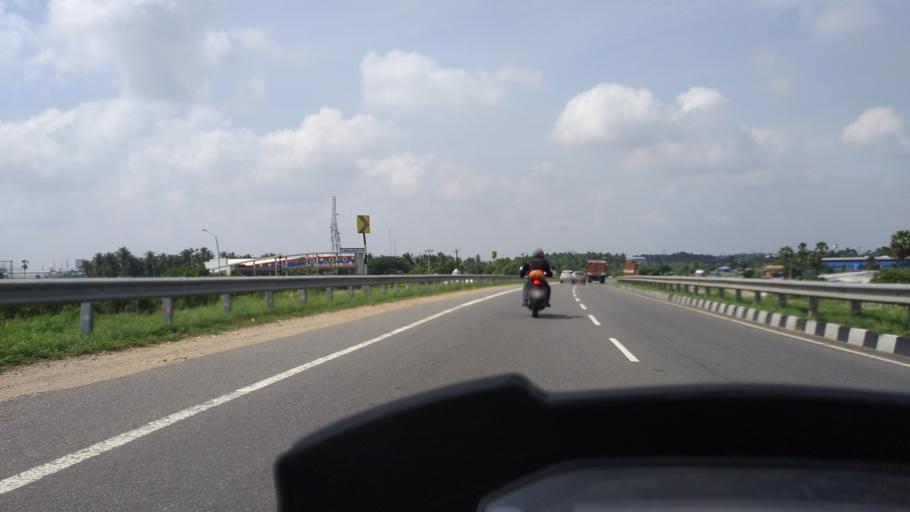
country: IN
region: Tamil Nadu
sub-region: Erode
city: Perundurai
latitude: 11.2584
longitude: 77.5501
